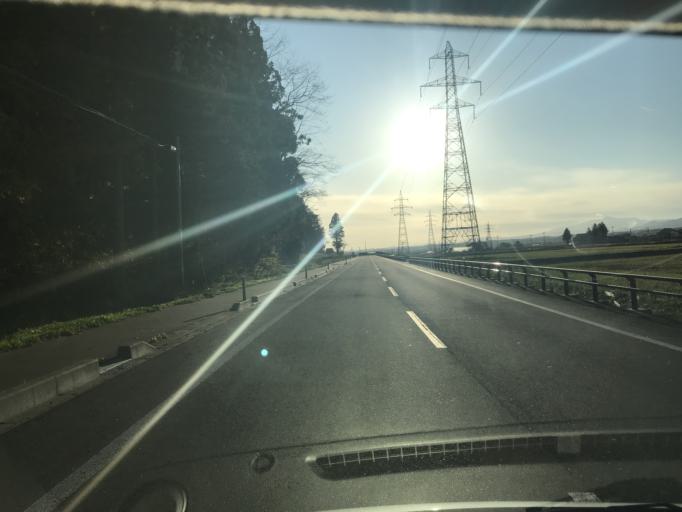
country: JP
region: Iwate
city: Mizusawa
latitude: 39.0726
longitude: 141.1874
